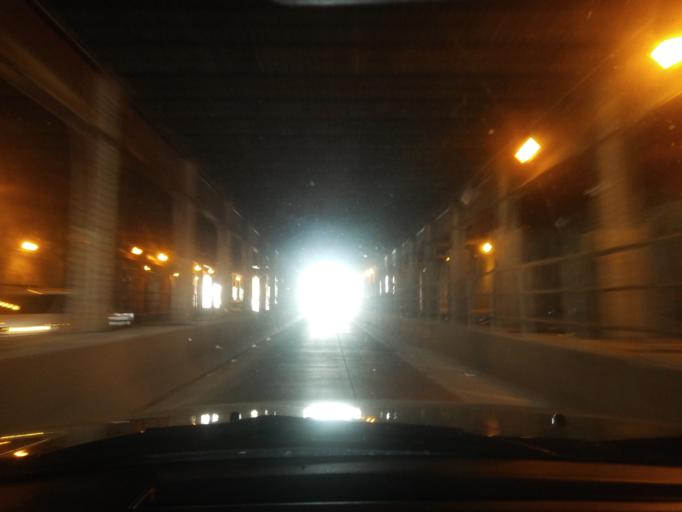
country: US
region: Illinois
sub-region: Cook County
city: Evergreen Park
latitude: 41.7792
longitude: -87.6792
